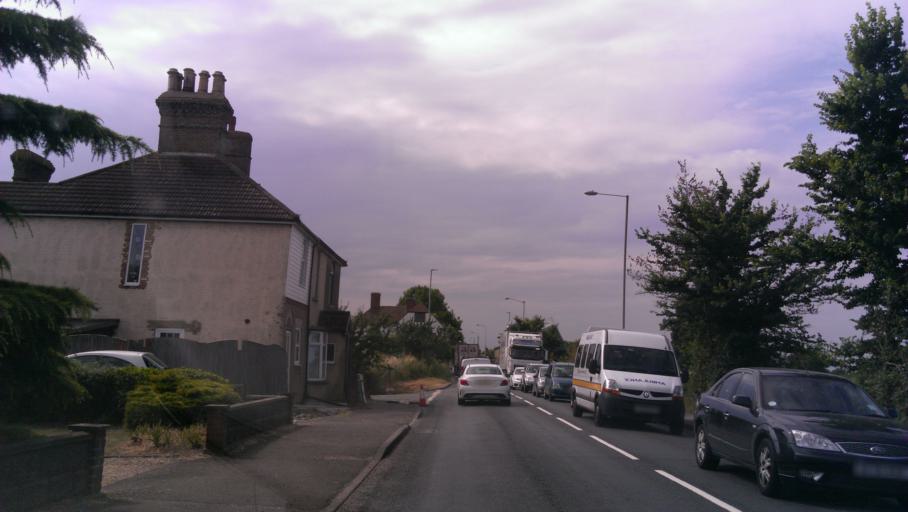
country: GB
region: England
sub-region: Kent
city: Teynham
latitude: 51.3298
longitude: 0.7914
